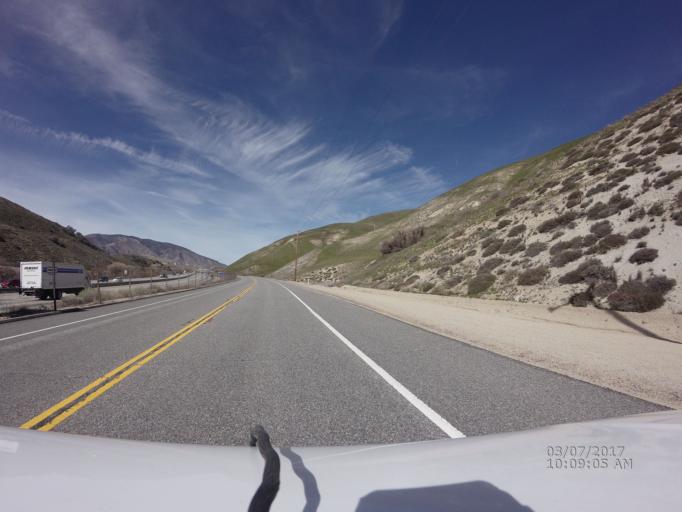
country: US
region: California
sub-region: Kern County
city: Lebec
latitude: 34.7932
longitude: -118.8366
